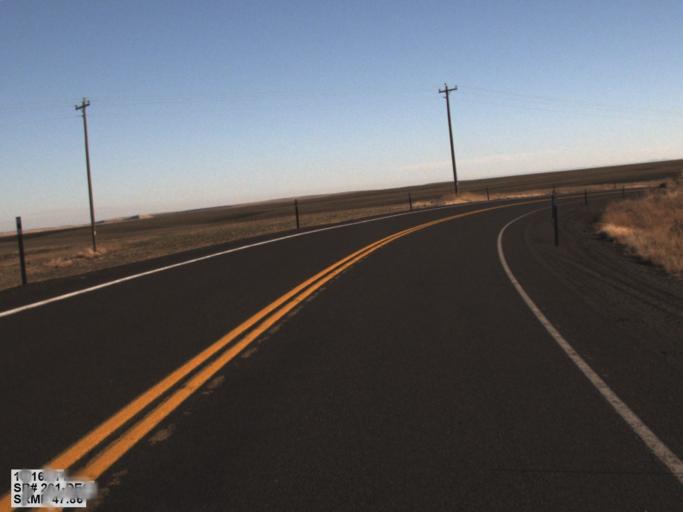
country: US
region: Washington
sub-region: Adams County
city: Ritzville
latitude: 46.9125
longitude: -118.3337
